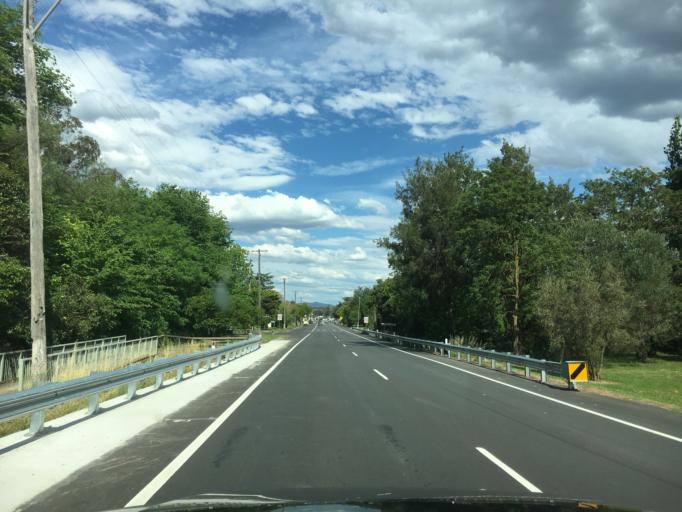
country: AU
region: New South Wales
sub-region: Liverpool Plains
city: Quirindi
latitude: -31.7600
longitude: 150.8284
